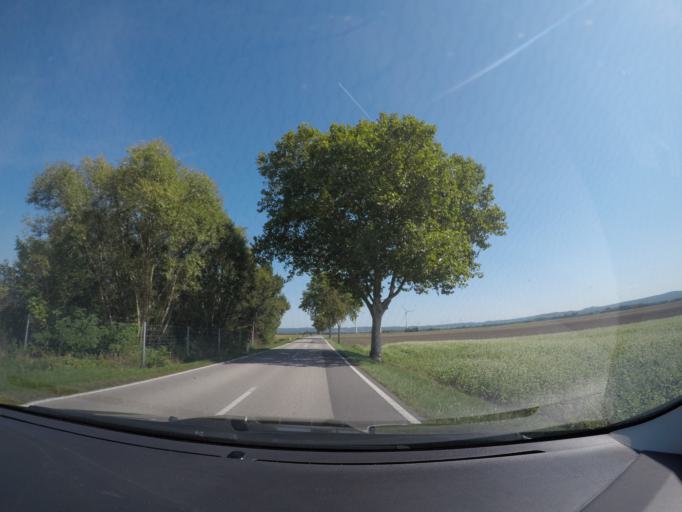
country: AT
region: Lower Austria
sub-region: Politischer Bezirk Baden
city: Mitterndorf an der Fischa
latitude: 47.9624
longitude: 16.4713
